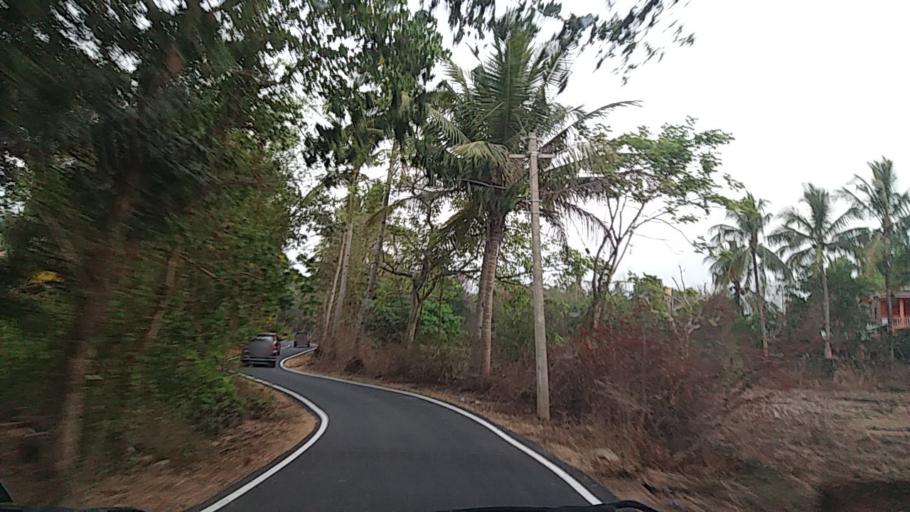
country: IN
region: Goa
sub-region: South Goa
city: Chinchinim
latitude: 15.2159
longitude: 73.9701
